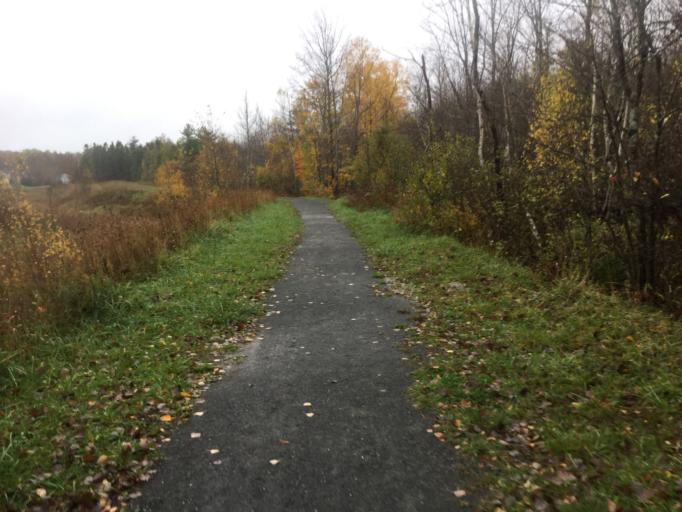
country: CA
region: Nova Scotia
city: New Glasgow
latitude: 45.5518
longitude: -62.6771
